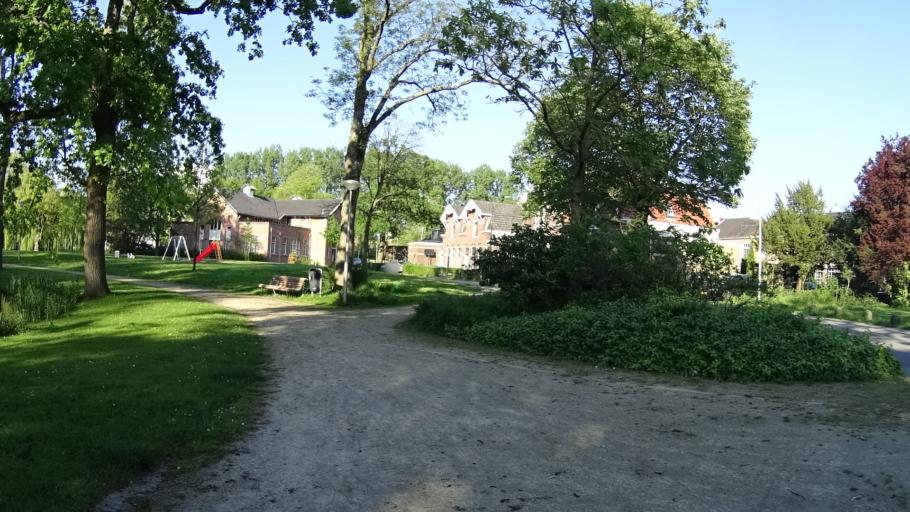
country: NL
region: South Holland
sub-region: Gemeente Delft
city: Delft
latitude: 52.0155
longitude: 4.3463
